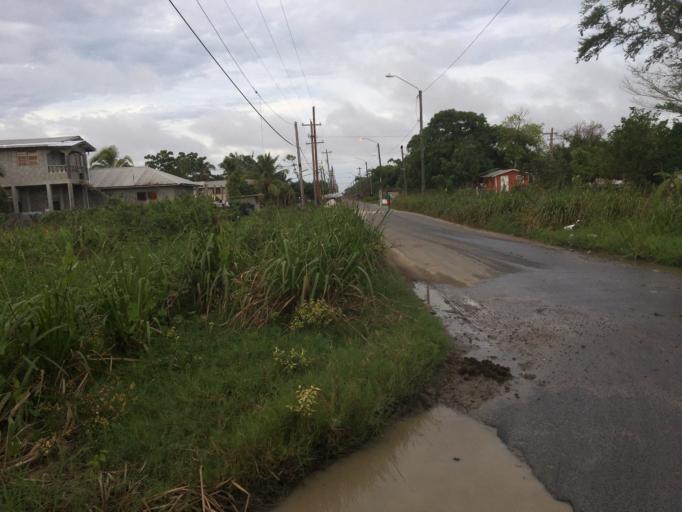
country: GY
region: Demerara-Mahaica
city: Georgetown
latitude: 6.7914
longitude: -58.1207
